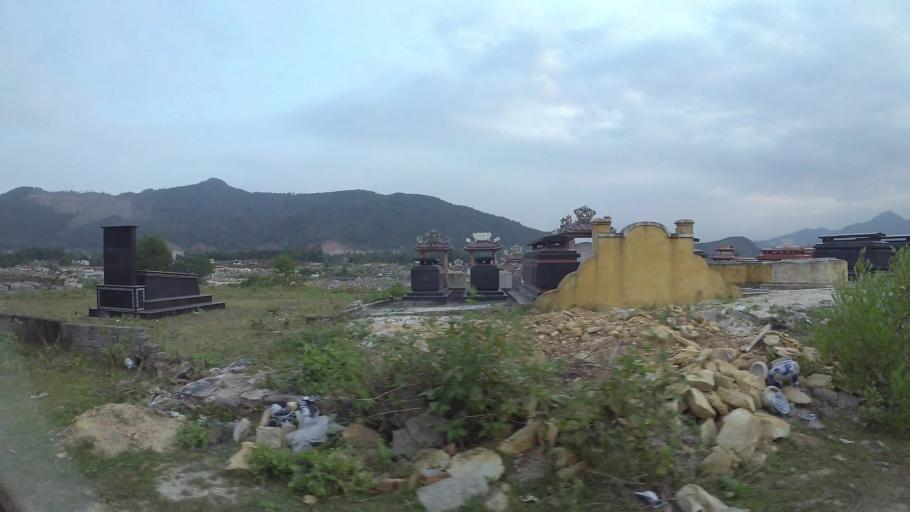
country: VN
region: Da Nang
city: Lien Chieu
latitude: 16.0621
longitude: 108.1167
